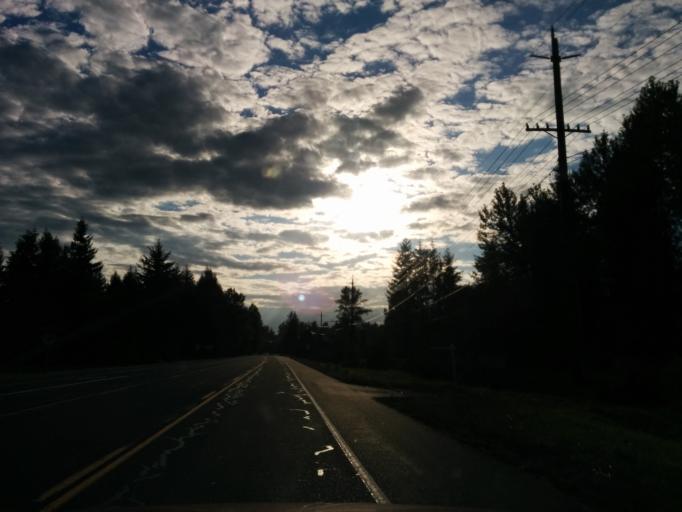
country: US
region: Washington
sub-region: Snohomish County
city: Sultan
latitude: 47.8665
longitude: -121.7895
